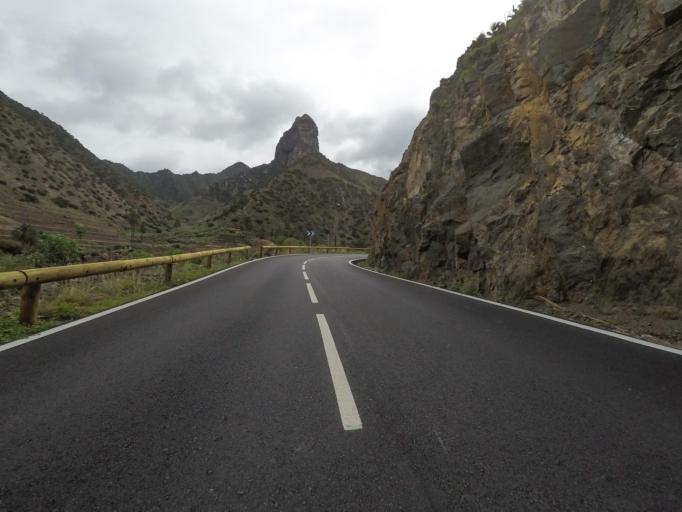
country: ES
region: Canary Islands
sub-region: Provincia de Santa Cruz de Tenerife
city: Vallehermosa
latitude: 28.1916
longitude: -17.2617
